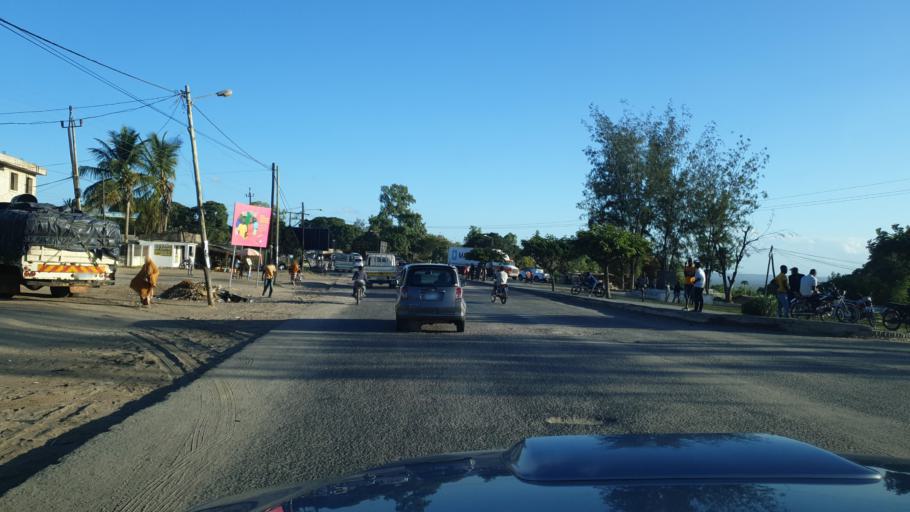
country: MZ
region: Nampula
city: Nacala
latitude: -14.5743
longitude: 40.6820
